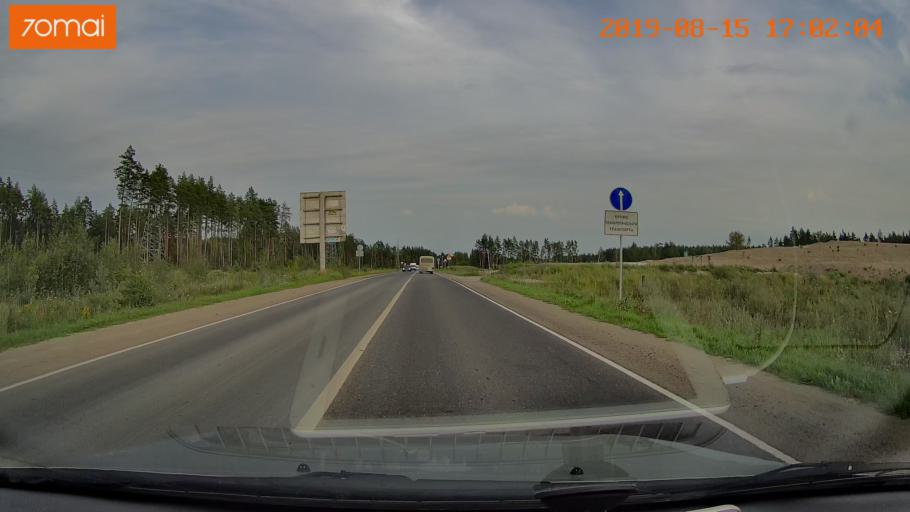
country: RU
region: Moskovskaya
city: Malyshevo
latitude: 55.4871
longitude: 38.3852
